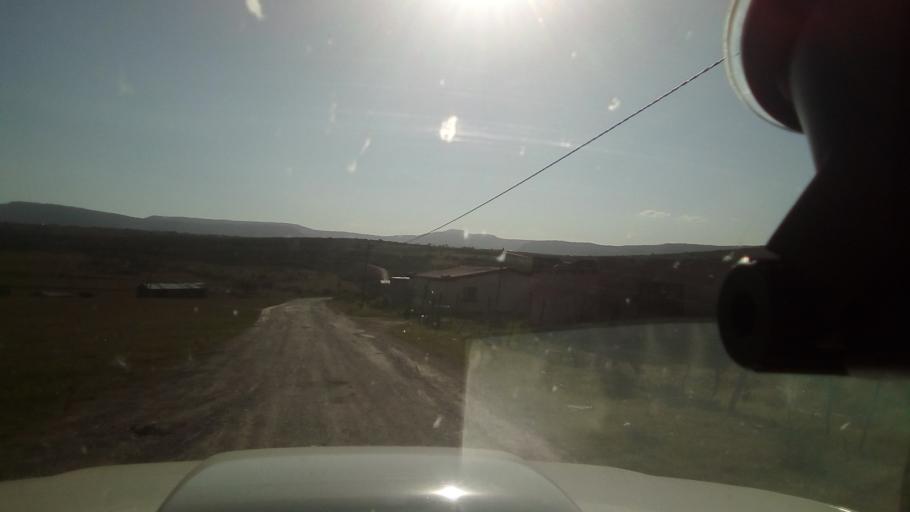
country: ZA
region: Eastern Cape
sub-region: Buffalo City Metropolitan Municipality
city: Bhisho
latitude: -32.7973
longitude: 27.3462
